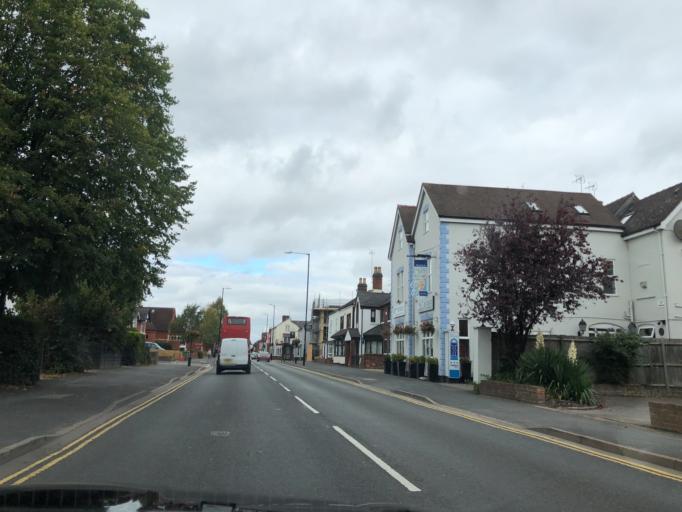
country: GB
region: England
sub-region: Warwickshire
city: Kenilworth
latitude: 52.3380
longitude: -1.5744
